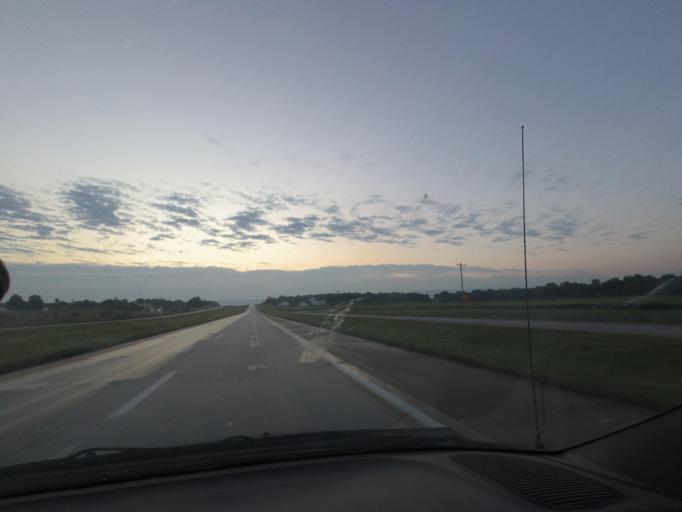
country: US
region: Missouri
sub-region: Macon County
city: Macon
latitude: 39.7595
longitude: -92.6739
